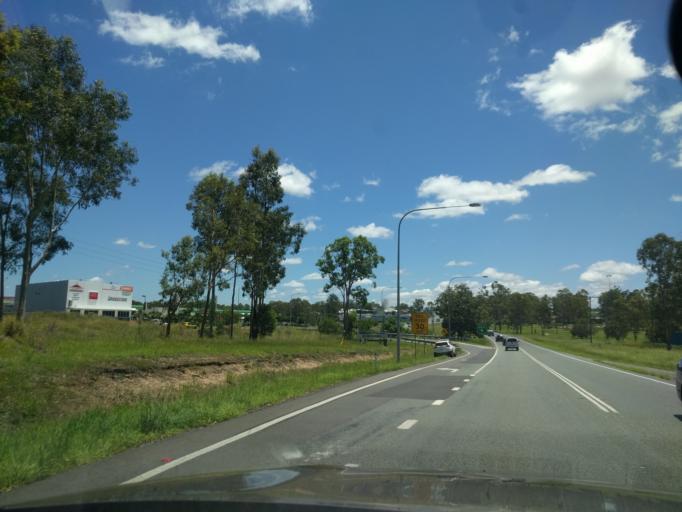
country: AU
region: Queensland
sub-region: Logan
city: Cedar Vale
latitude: -27.8383
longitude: 153.0256
